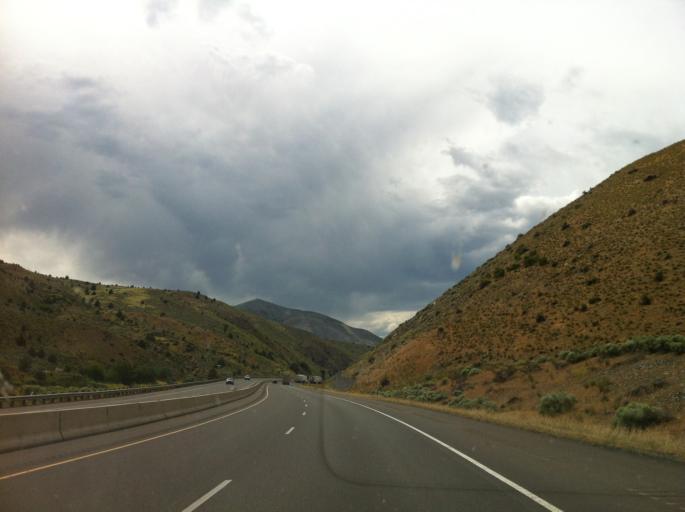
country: US
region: Idaho
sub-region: Washington County
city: Weiser
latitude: 44.4846
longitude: -117.3541
